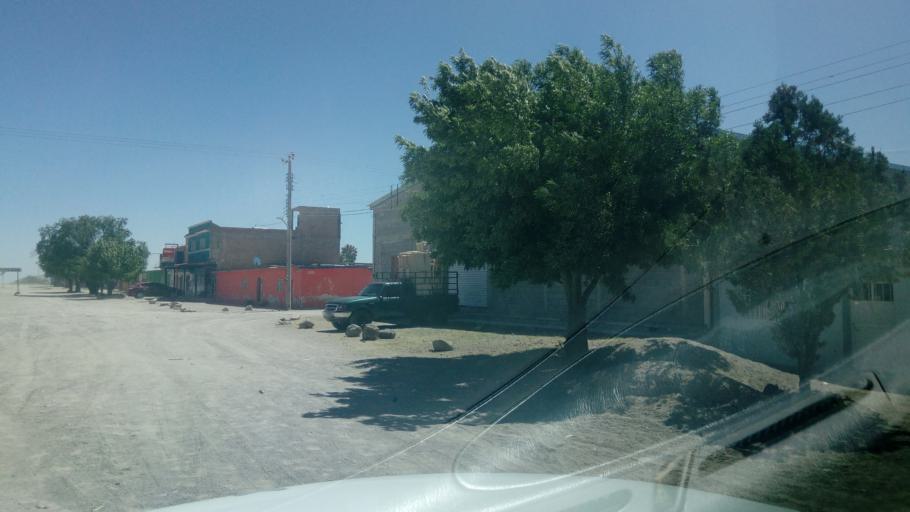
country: MX
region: Durango
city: Victoria de Durango
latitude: 24.1703
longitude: -104.7021
